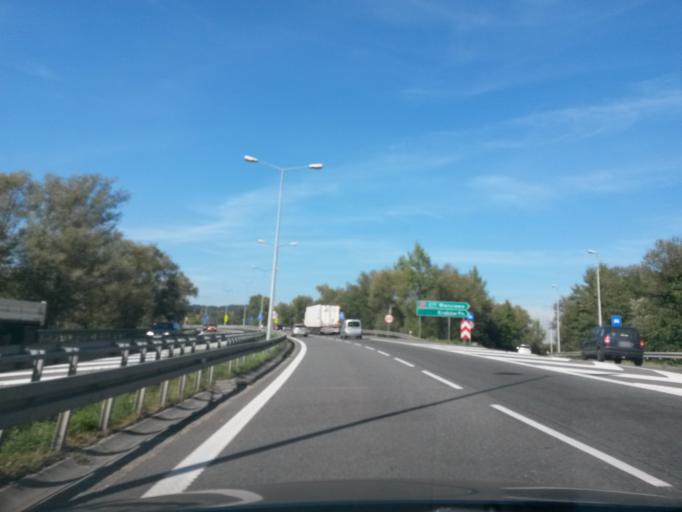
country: PL
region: Lesser Poland Voivodeship
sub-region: Powiat krakowski
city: Balice
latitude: 50.0855
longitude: 19.8076
